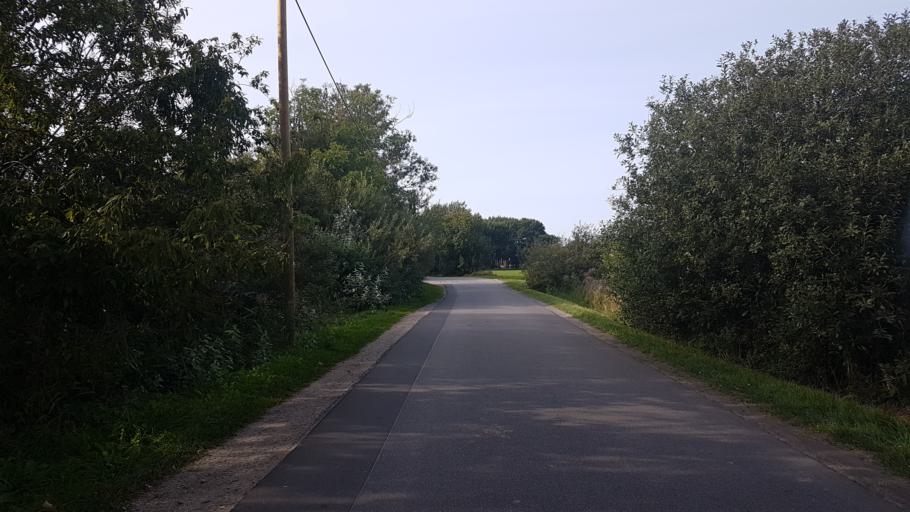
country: DE
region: Mecklenburg-Vorpommern
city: Hiddensee
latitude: 54.4580
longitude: 13.1393
